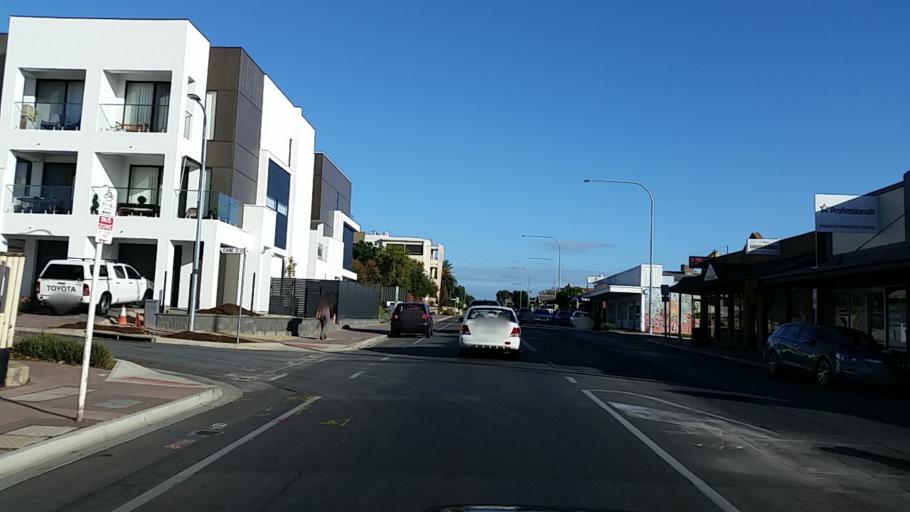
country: AU
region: South Australia
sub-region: Prospect
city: Prospect
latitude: -34.8816
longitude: 138.5937
